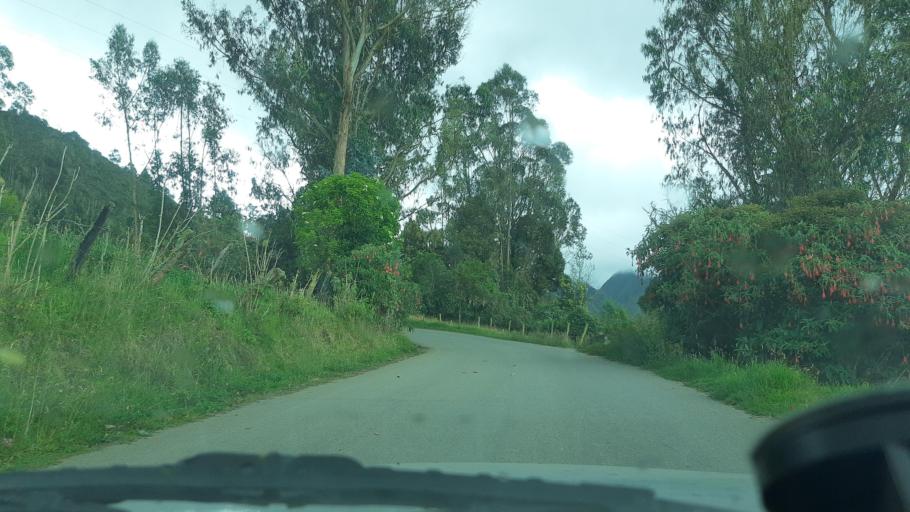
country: CO
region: Cundinamarca
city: Umbita
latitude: 5.2177
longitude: -73.4688
